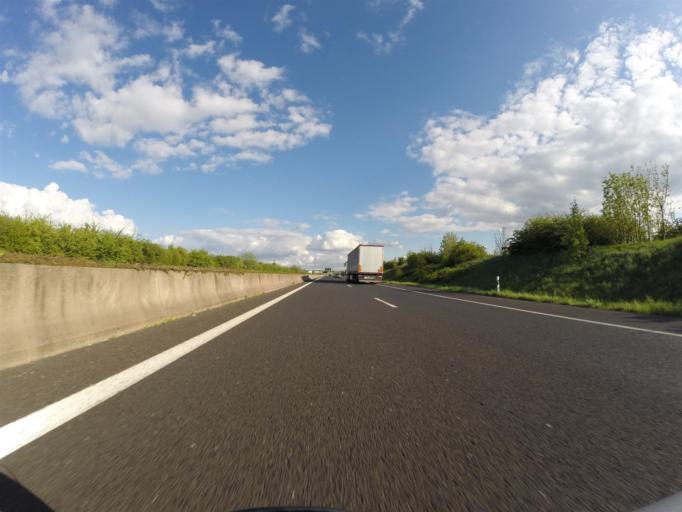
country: LU
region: Grevenmacher
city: Schengen
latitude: 49.4879
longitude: 6.3328
